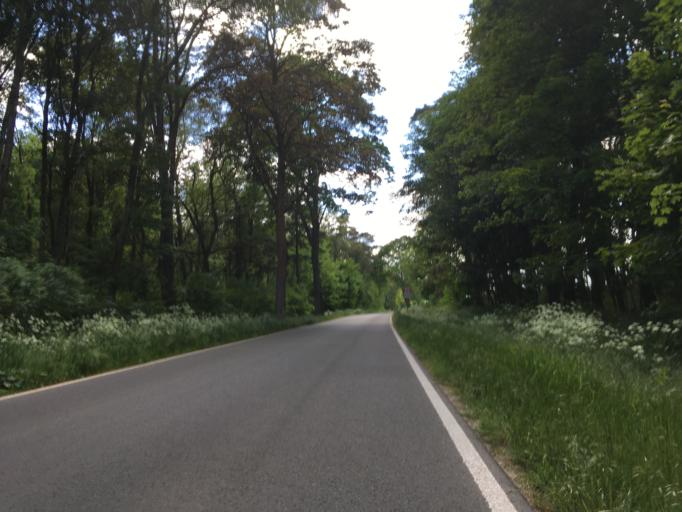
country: DE
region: Brandenburg
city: Protzel
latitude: 52.5979
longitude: 13.9753
